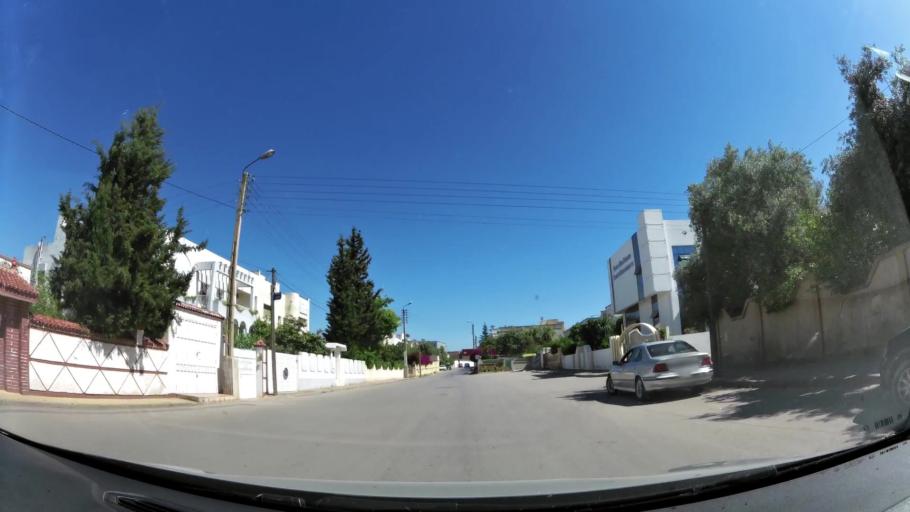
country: MA
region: Fes-Boulemane
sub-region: Fes
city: Fes
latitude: 34.0184
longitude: -4.9920
